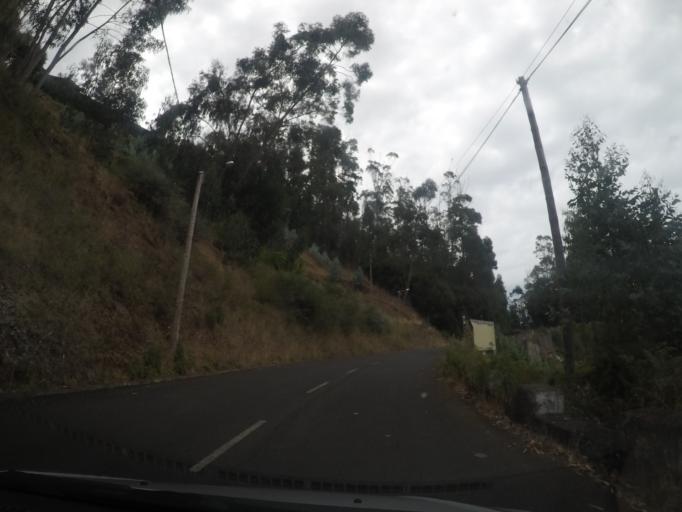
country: PT
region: Madeira
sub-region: Santa Cruz
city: Camacha
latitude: 32.6879
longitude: -16.8296
